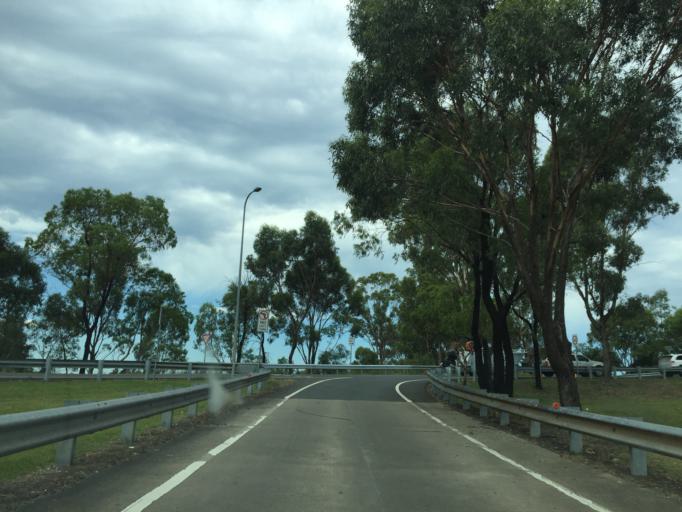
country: AU
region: New South Wales
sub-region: Blacktown
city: Doonside
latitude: -33.8009
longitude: 150.8881
